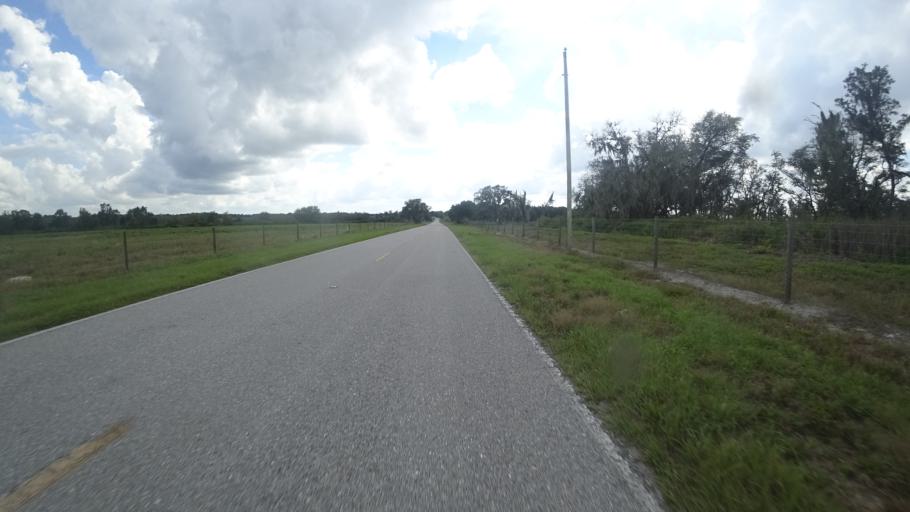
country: US
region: Florida
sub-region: Hillsborough County
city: Wimauma
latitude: 27.6263
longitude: -82.2310
